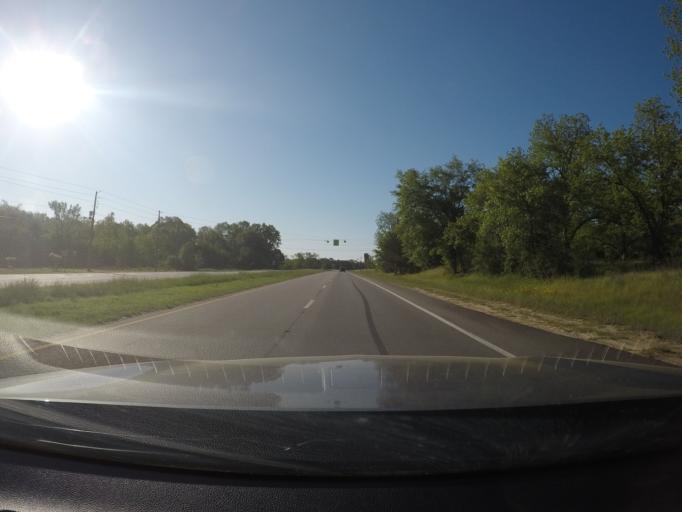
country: US
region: Georgia
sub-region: Bulloch County
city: Statesboro
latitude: 32.4940
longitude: -81.8155
